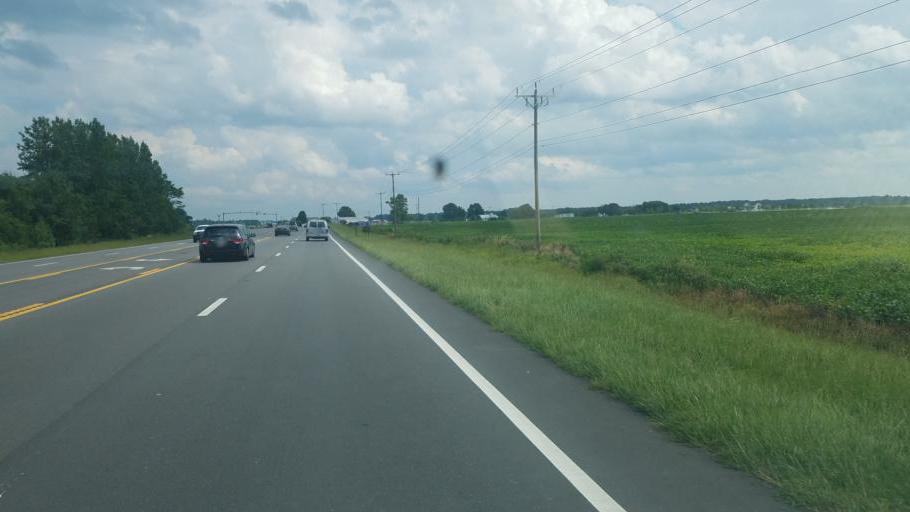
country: US
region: North Carolina
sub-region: Currituck County
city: Moyock
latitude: 36.5113
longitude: -76.1629
